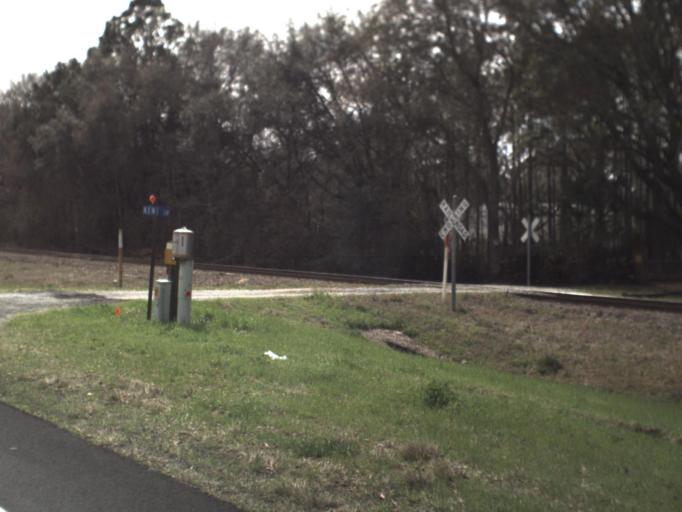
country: US
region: Florida
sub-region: Washington County
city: Chipley
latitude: 30.6787
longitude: -85.3939
